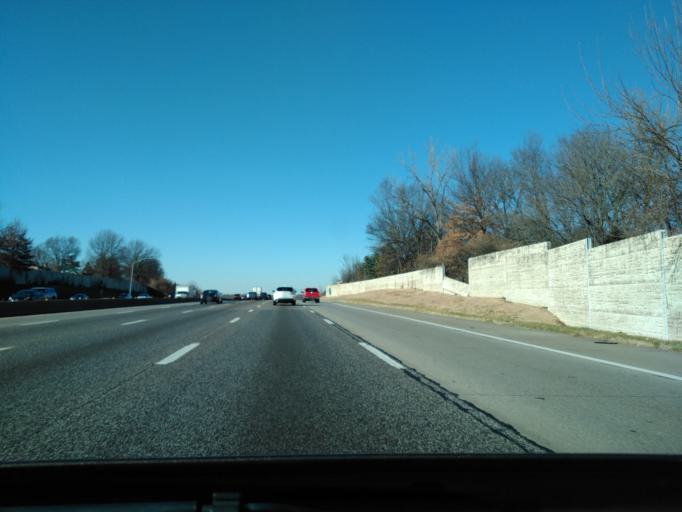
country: US
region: Missouri
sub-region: Saint Louis County
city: Sappington
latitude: 38.5209
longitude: -90.3930
